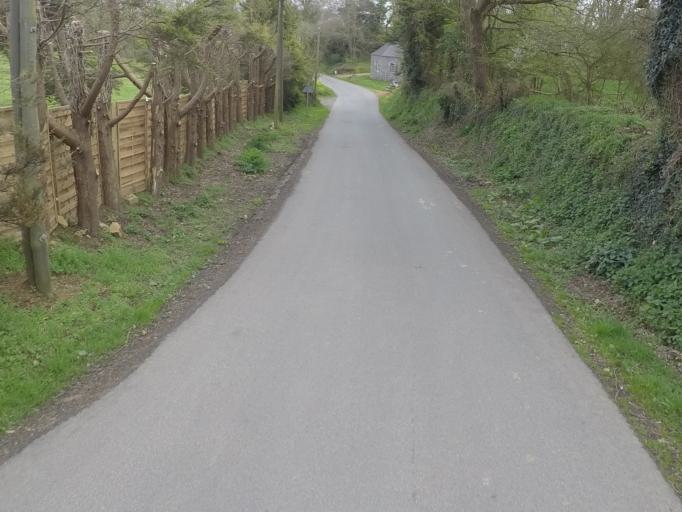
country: FR
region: Brittany
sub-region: Departement des Cotes-d'Armor
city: Plouha
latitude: 48.7044
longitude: -2.9352
